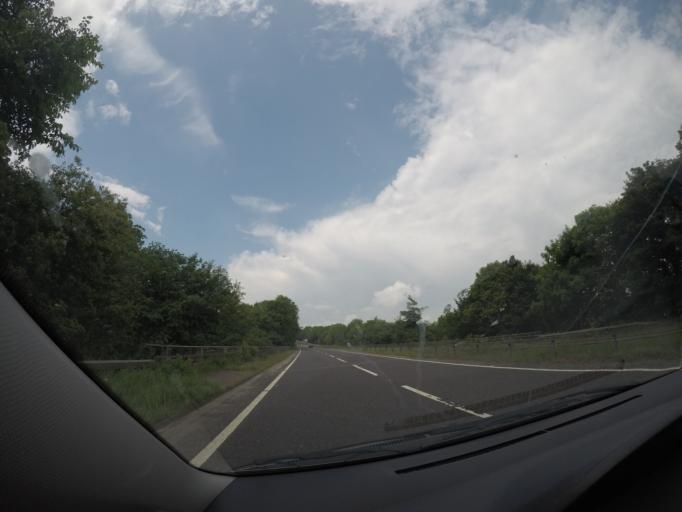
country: GB
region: England
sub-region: County Durham
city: Rokeby
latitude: 54.5147
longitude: -1.8668
